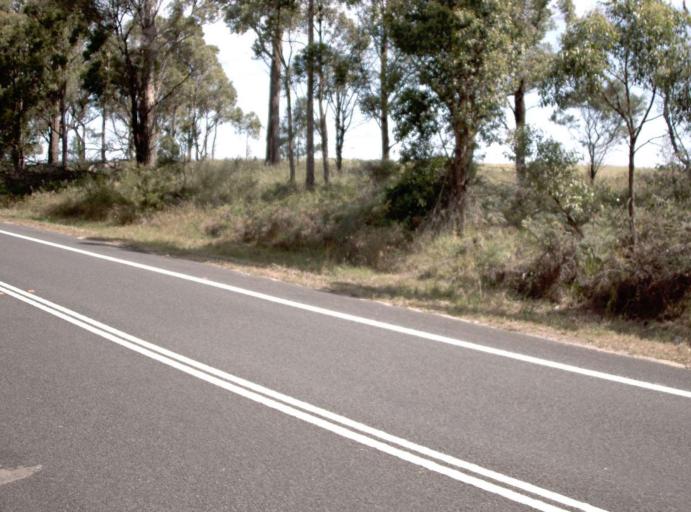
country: AU
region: Victoria
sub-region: East Gippsland
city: Lakes Entrance
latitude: -37.8288
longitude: 147.8987
